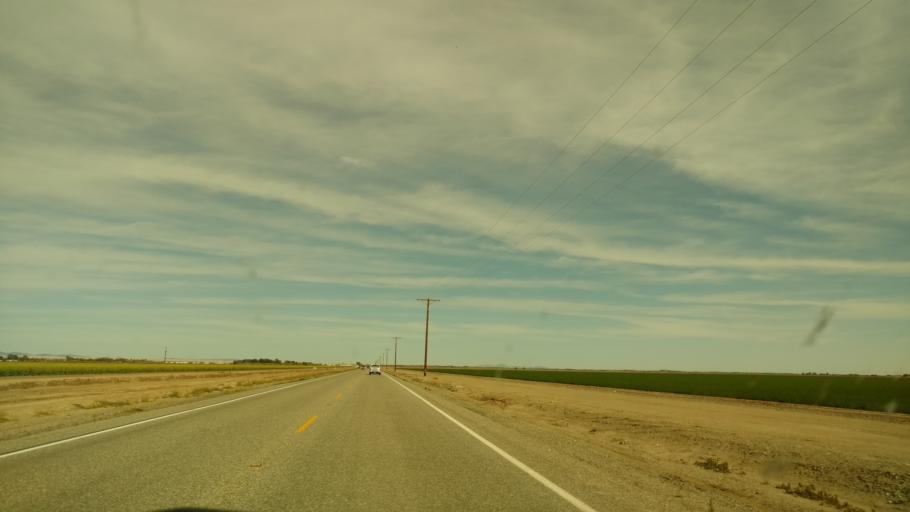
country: US
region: California
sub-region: Imperial County
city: Holtville
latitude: 32.9748
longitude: -115.3450
